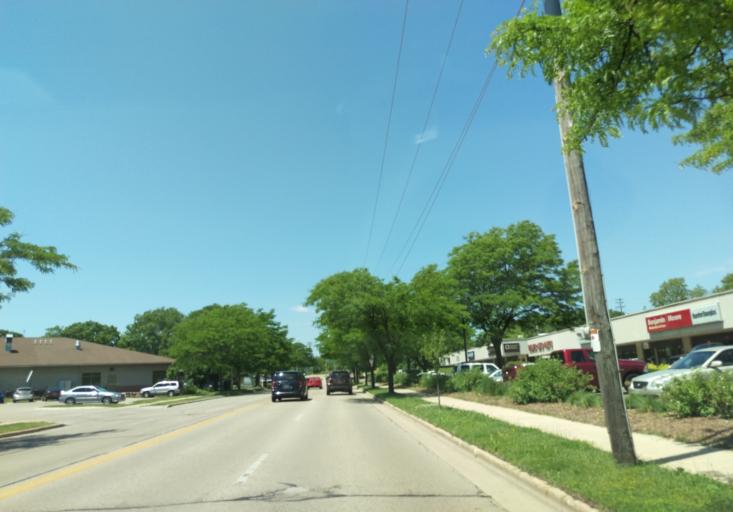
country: US
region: Wisconsin
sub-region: Dane County
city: Shorewood Hills
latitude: 43.0525
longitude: -89.4835
